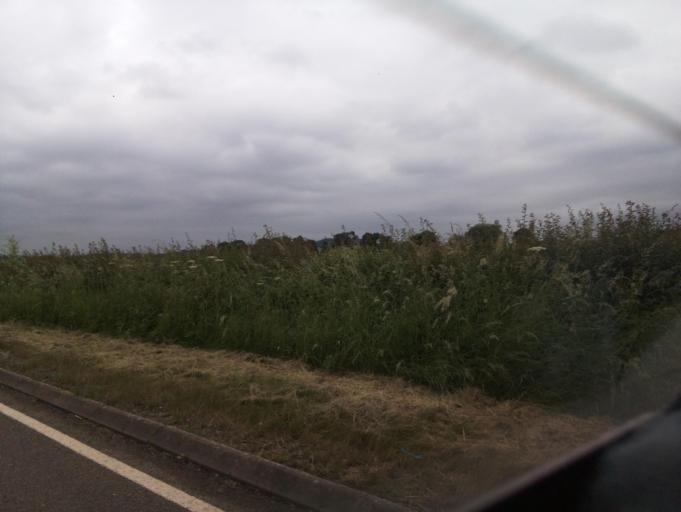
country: GB
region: England
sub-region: Leicestershire
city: Melton Mowbray
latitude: 52.7336
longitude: -0.8497
